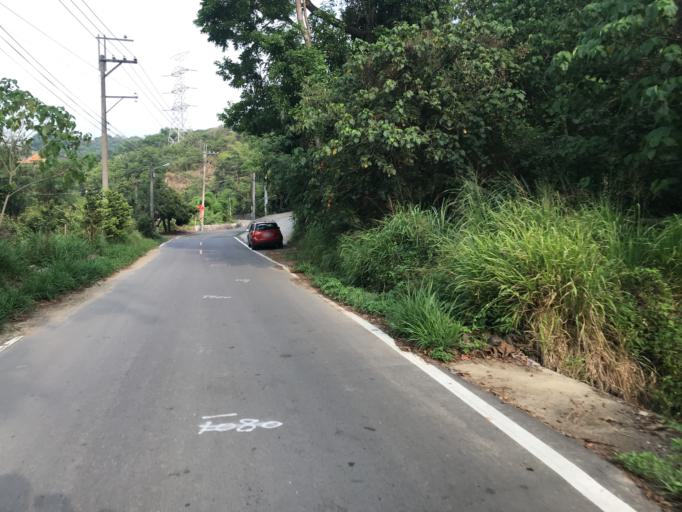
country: TW
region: Taiwan
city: Zhongxing New Village
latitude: 24.0380
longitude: 120.7103
